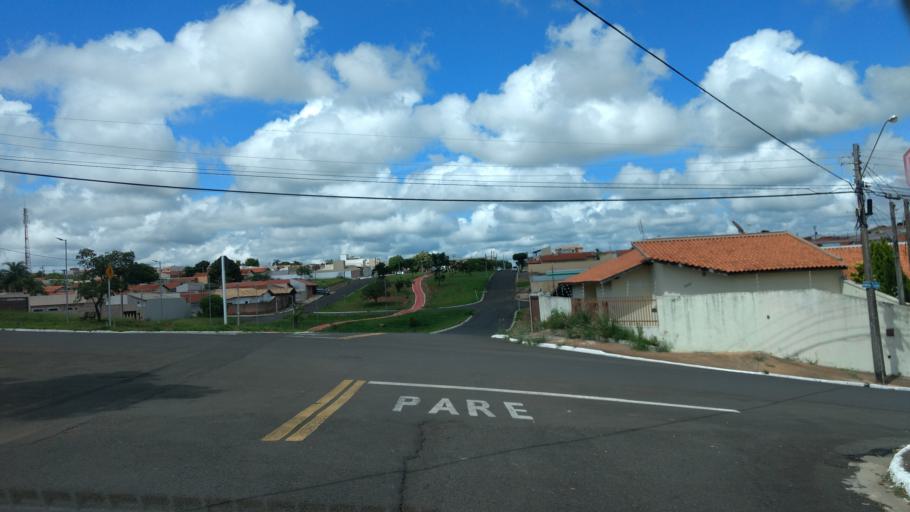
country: BR
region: Sao Paulo
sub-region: Botucatu
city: Botucatu
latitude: -22.8560
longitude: -48.4455
